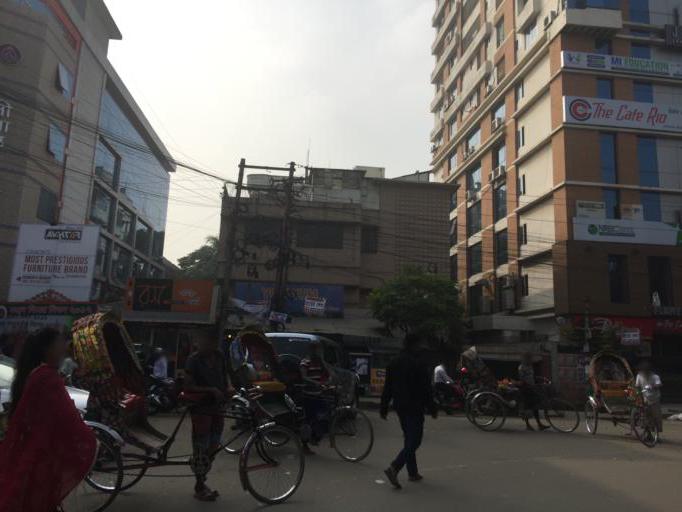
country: BD
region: Dhaka
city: Azimpur
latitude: 23.7383
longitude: 90.3761
